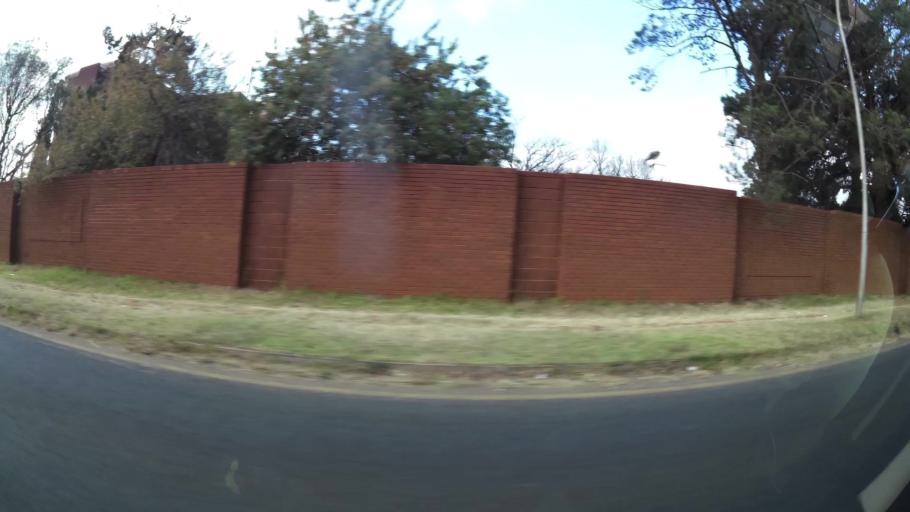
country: ZA
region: Gauteng
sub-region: Ekurhuleni Metropolitan Municipality
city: Benoni
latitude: -26.1606
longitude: 28.3055
